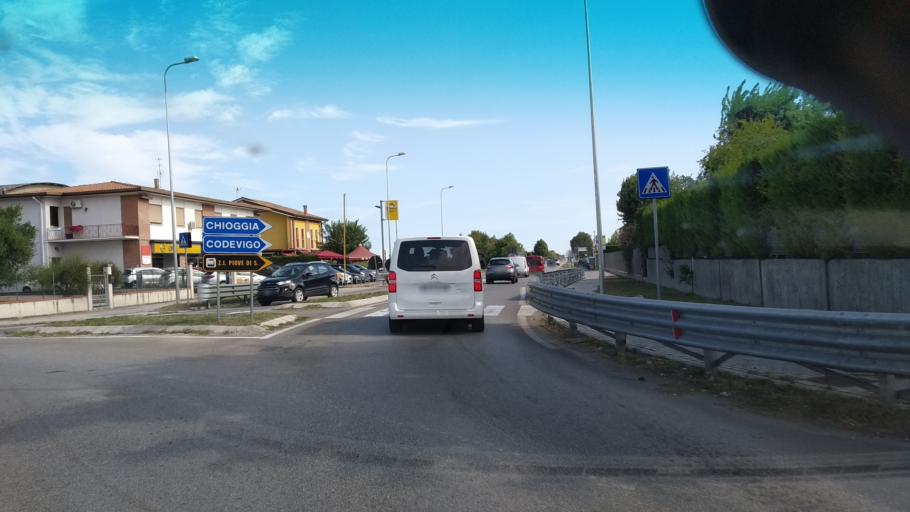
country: IT
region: Veneto
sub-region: Provincia di Padova
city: Piove di Sacco-Piovega
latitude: 45.2957
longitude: 12.0543
